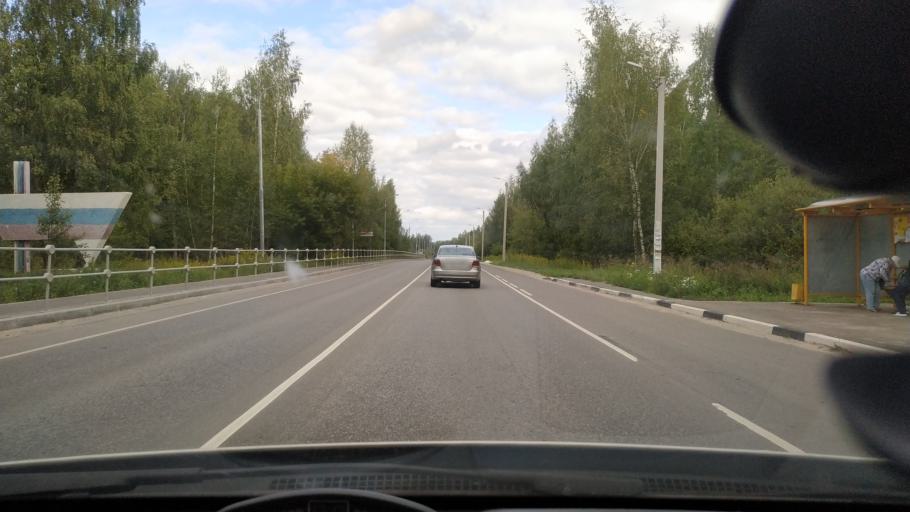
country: RU
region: Moskovskaya
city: Likino-Dulevo
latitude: 55.7265
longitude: 38.9693
